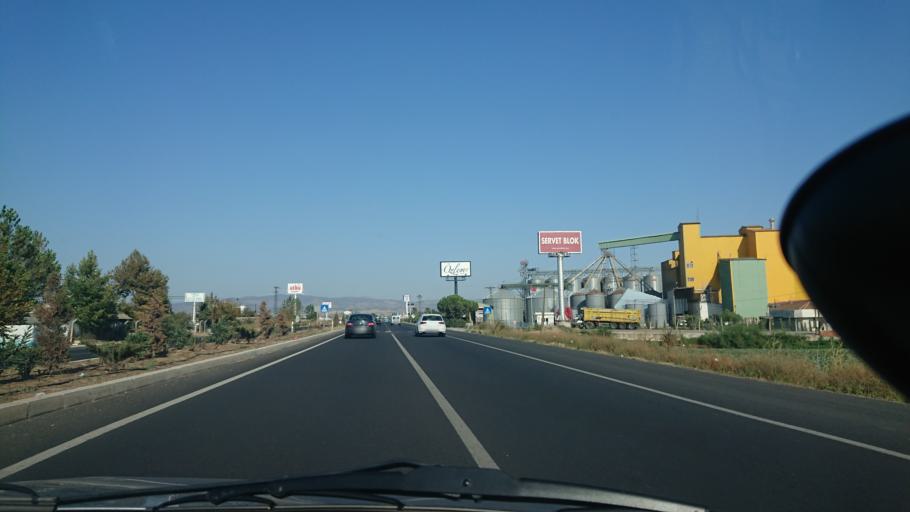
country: TR
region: Manisa
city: Salihli
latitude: 38.5040
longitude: 28.2215
